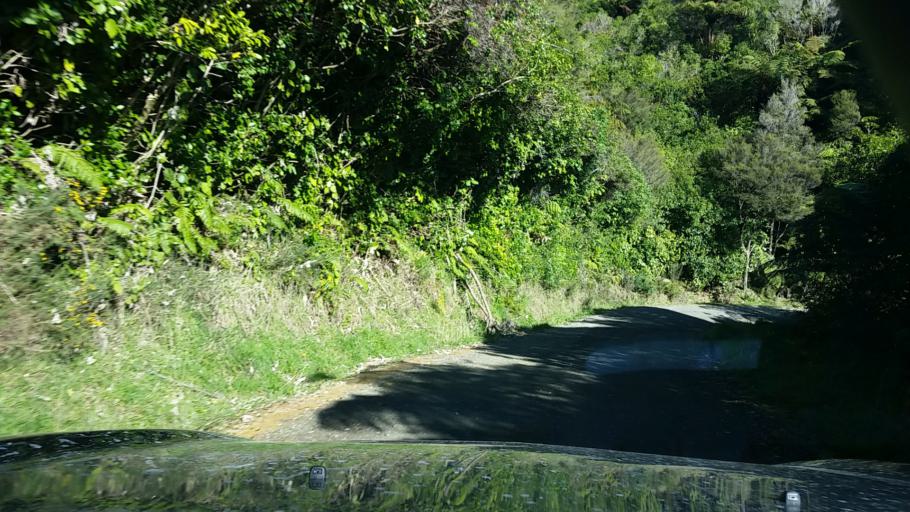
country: NZ
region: Marlborough
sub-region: Marlborough District
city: Picton
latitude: -41.1341
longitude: 174.0470
